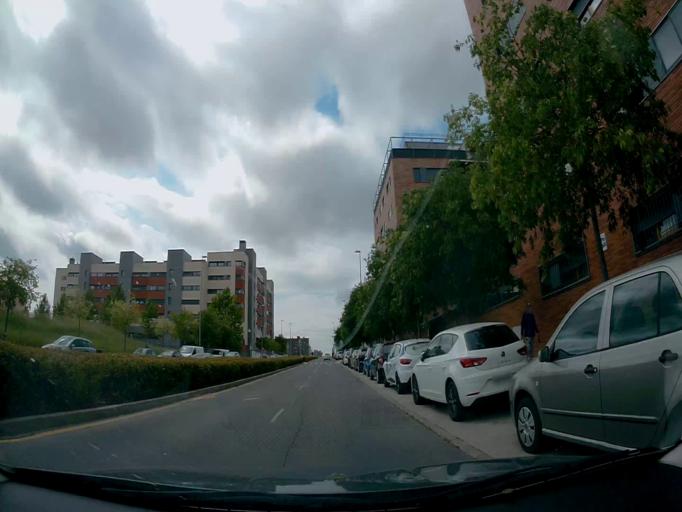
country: ES
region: Madrid
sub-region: Provincia de Madrid
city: Alcorcon
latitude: 40.3324
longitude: -3.8350
